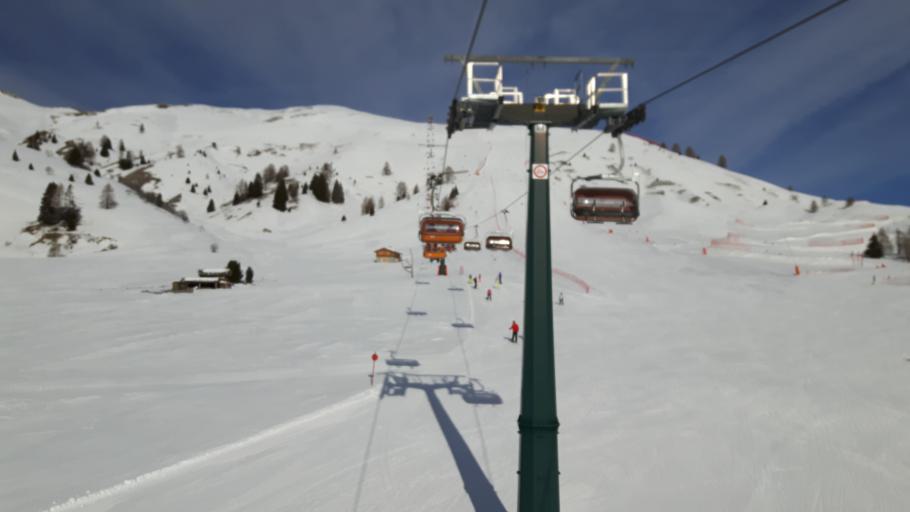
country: IT
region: Trentino-Alto Adige
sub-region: Provincia di Trento
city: Moena
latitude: 46.3346
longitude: 11.6992
